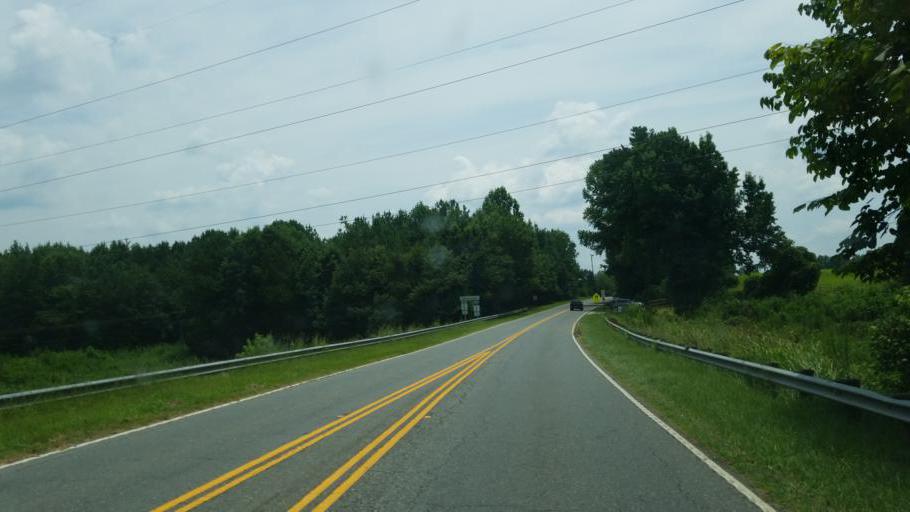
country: US
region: South Carolina
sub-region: York County
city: York
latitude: 35.0096
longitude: -81.2619
